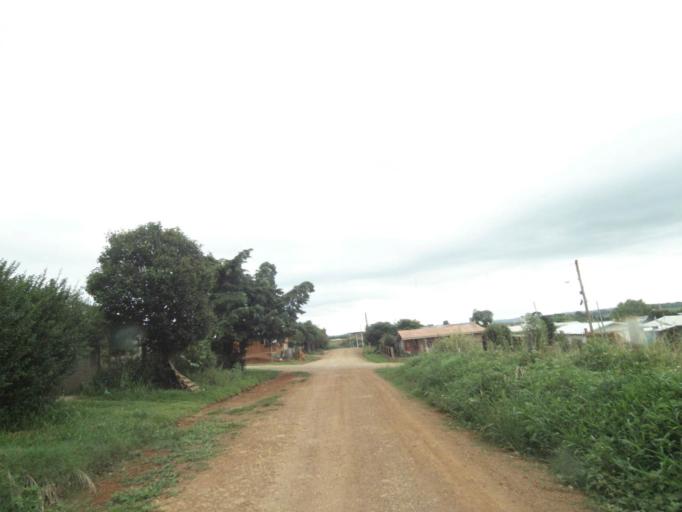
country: BR
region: Rio Grande do Sul
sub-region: Lagoa Vermelha
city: Lagoa Vermelha
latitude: -28.2001
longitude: -51.5315
